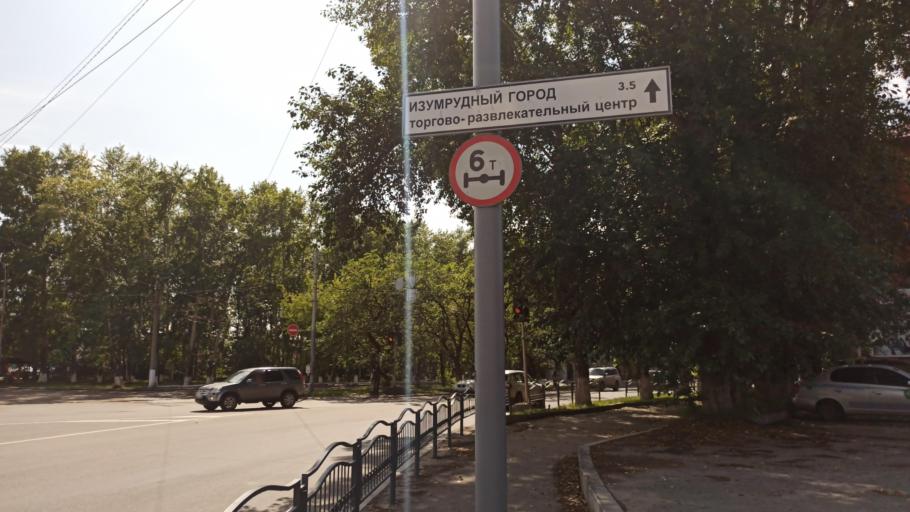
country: RU
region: Tomsk
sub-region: Tomskiy Rayon
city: Tomsk
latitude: 56.4763
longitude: 85.0159
